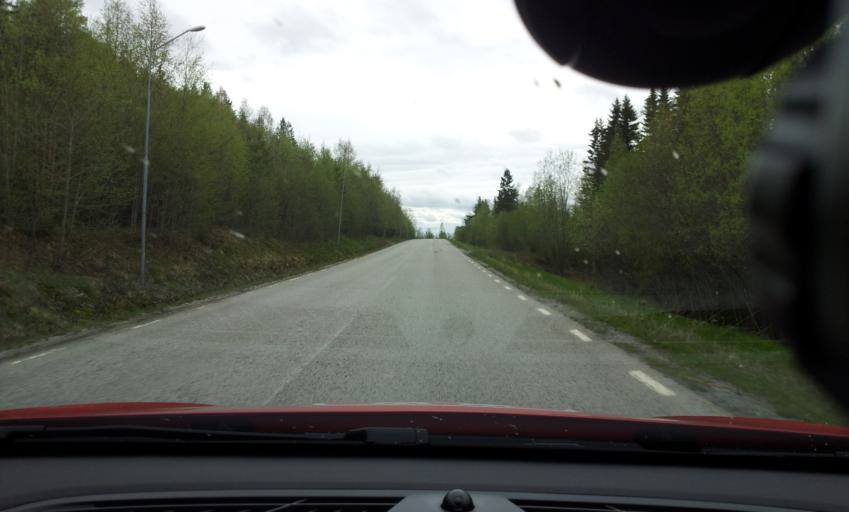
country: SE
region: Jaemtland
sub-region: Bergs Kommun
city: Hoverberg
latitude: 62.7692
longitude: 14.5463
